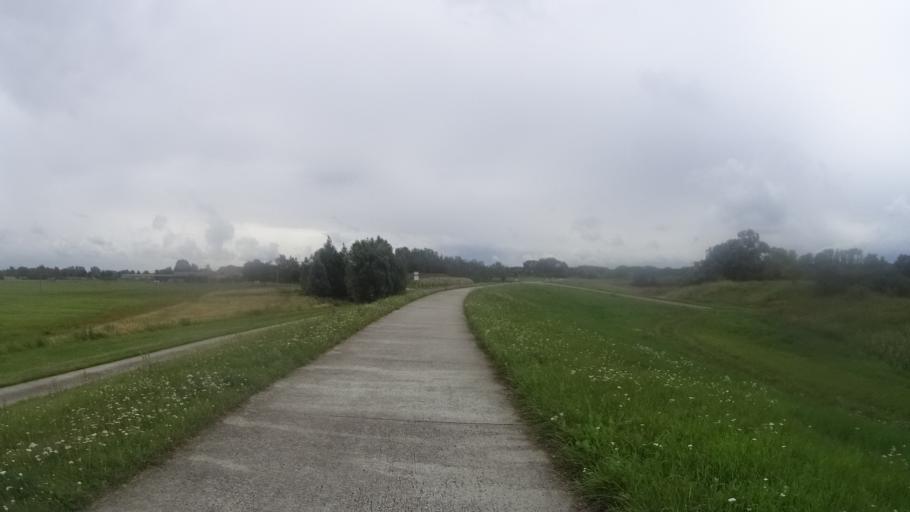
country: DE
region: Lower Saxony
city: Bleckede
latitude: 53.2939
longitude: 10.7946
